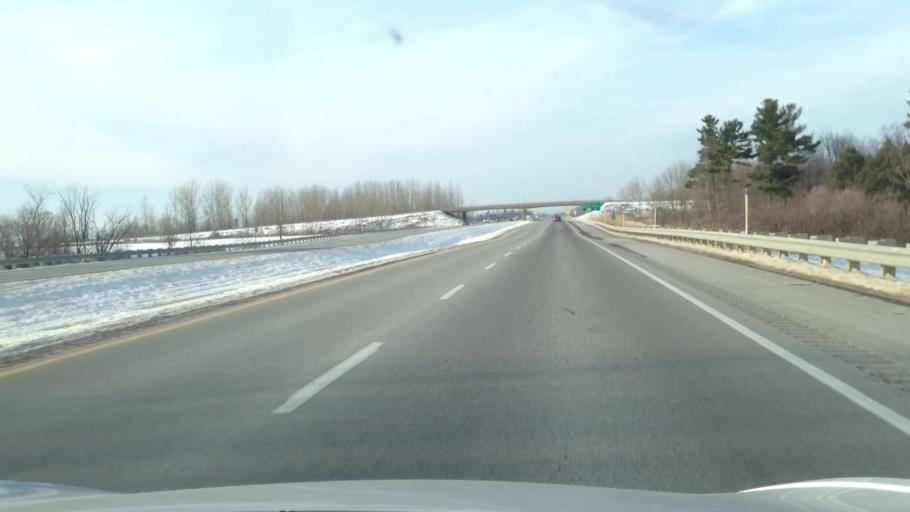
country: CA
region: Quebec
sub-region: Monteregie
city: Rigaud
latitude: 45.4899
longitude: -74.3463
